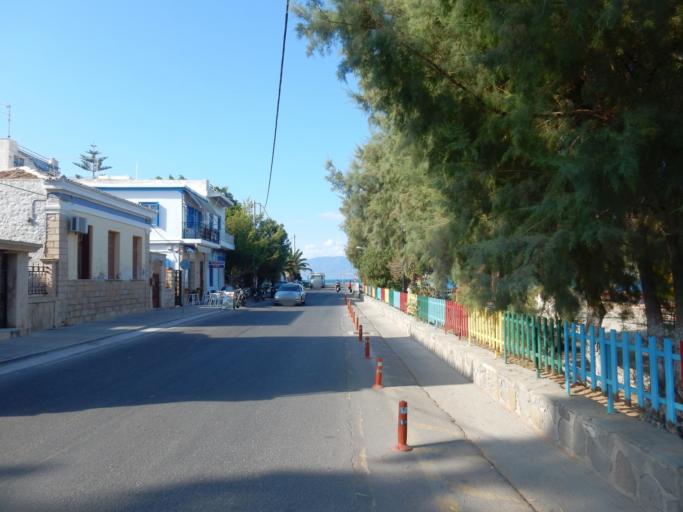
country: GR
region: Attica
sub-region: Nomos Piraios
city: Aegina
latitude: 37.7416
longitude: 23.4303
